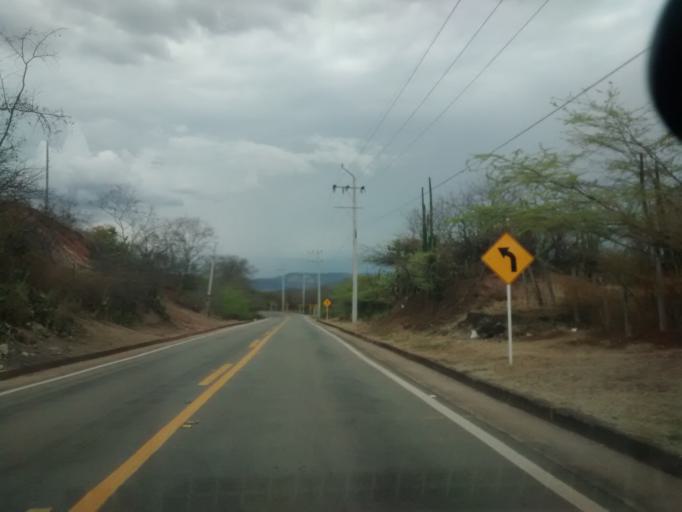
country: CO
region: Cundinamarca
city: Agua de Dios
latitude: 4.4279
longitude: -74.6935
